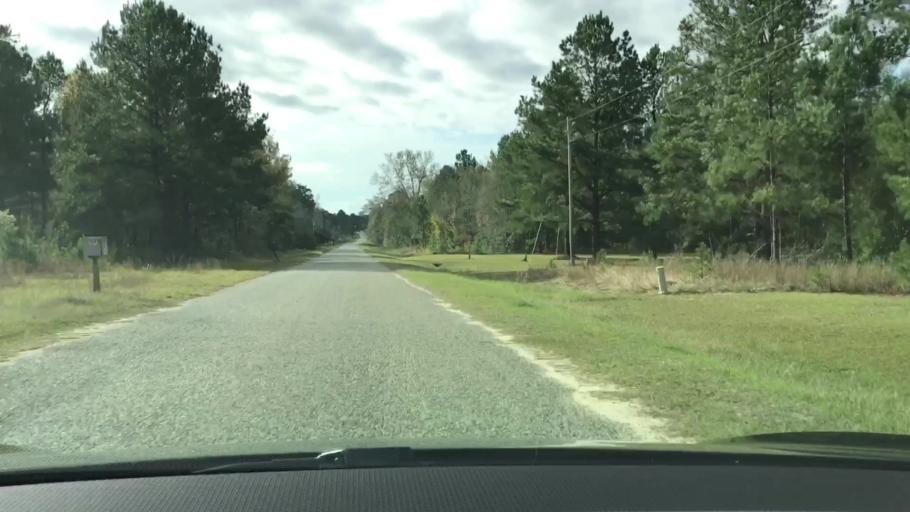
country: US
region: Georgia
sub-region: Jefferson County
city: Wadley
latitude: 32.8079
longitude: -82.3449
